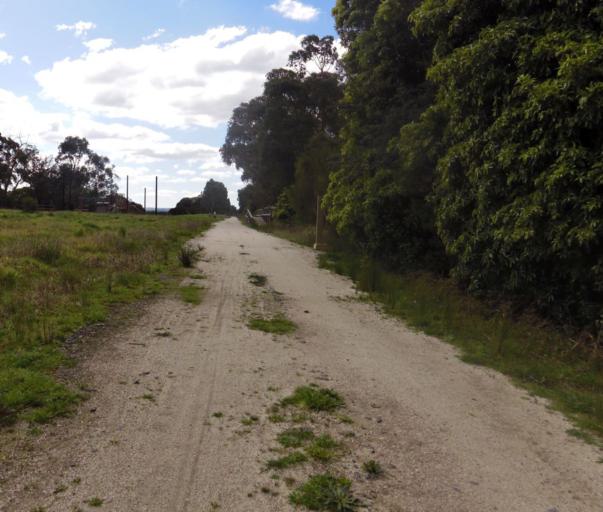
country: AU
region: Victoria
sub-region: Bass Coast
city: North Wonthaggi
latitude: -38.6542
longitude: 146.0278
